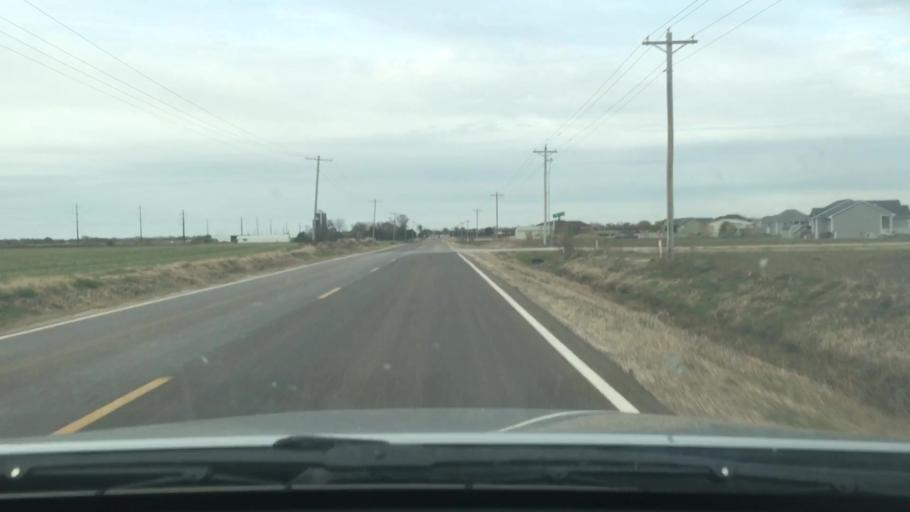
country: US
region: Kansas
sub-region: Sedgwick County
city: Colwich
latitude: 37.8105
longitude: -97.5186
